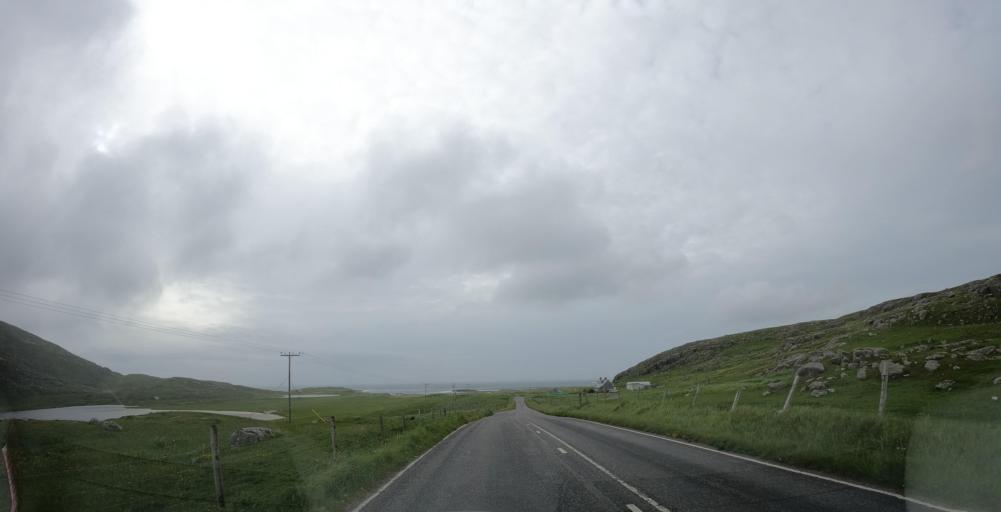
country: GB
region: Scotland
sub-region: Eilean Siar
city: Barra
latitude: 56.9667
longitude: -7.5139
